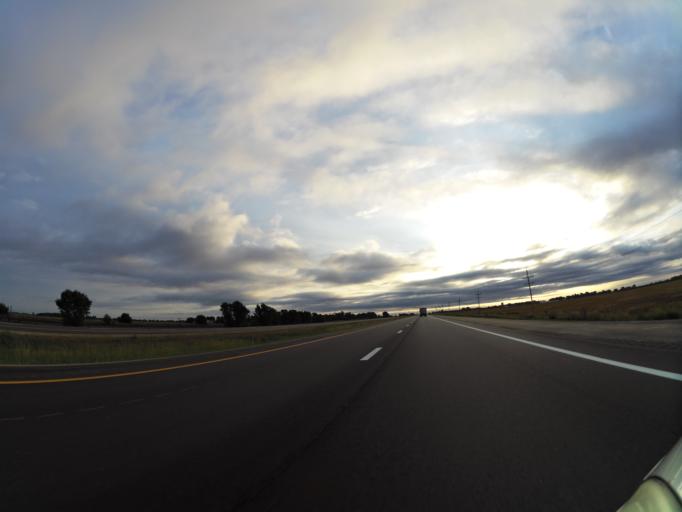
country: US
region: Kansas
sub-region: Reno County
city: South Hutchinson
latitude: 38.0079
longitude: -98.0118
